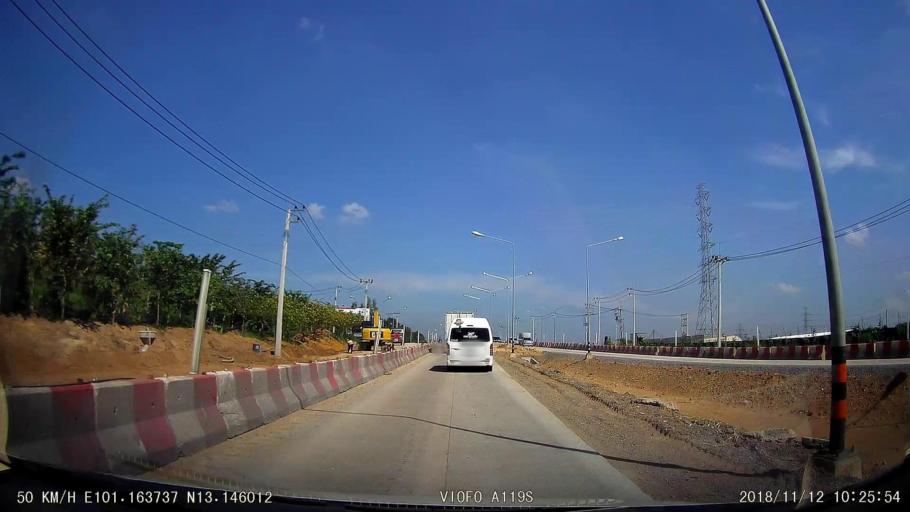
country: TH
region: Chon Buri
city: Ban Bueng
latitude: 13.1463
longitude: 101.1637
